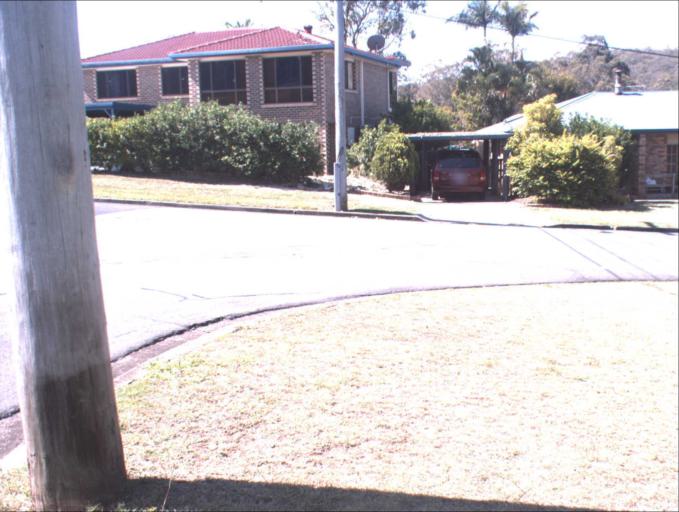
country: AU
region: Queensland
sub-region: Logan
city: Springwood
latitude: -27.6316
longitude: 153.1372
